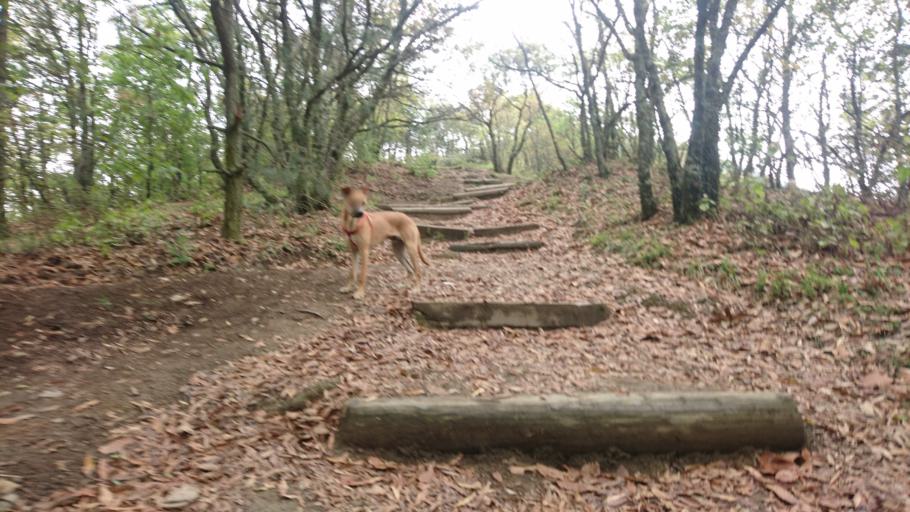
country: MX
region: Nuevo Leon
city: Garza Garcia
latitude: 25.5995
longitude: -100.3347
